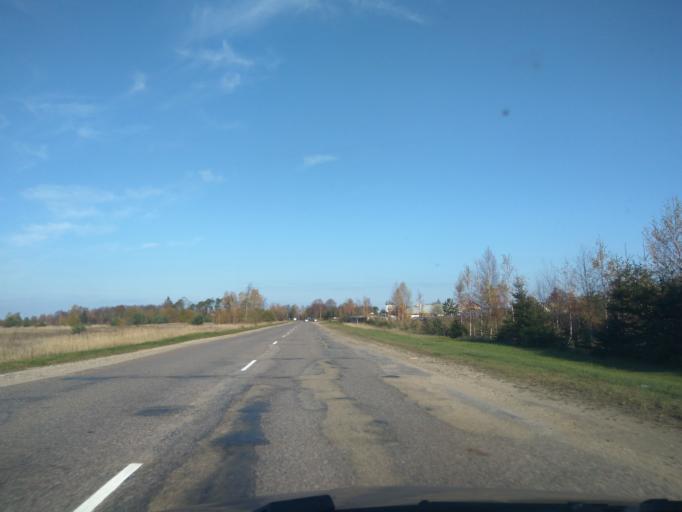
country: LV
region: Ventspils
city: Ventspils
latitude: 57.3381
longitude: 21.5660
